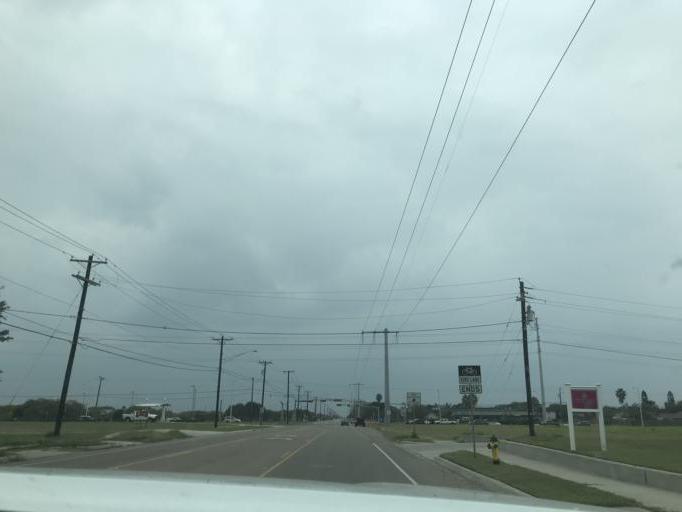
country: US
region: Texas
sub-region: Nueces County
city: Corpus Christi
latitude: 27.6769
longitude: -97.3497
